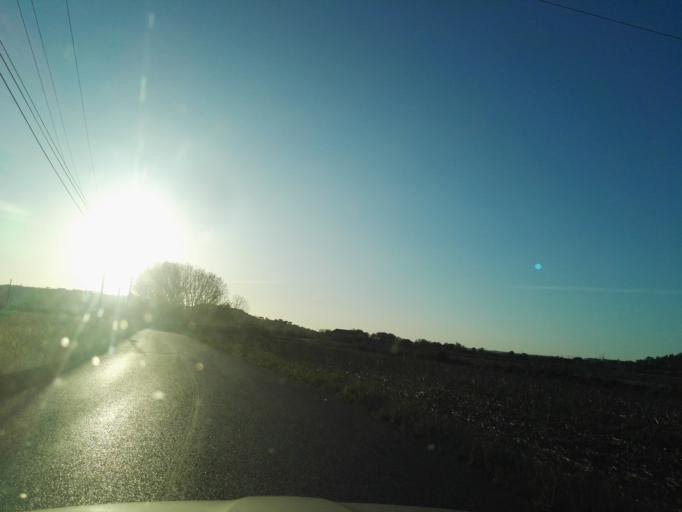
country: PT
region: Santarem
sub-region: Alpiarca
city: Alpiarca
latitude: 39.3398
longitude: -8.5712
